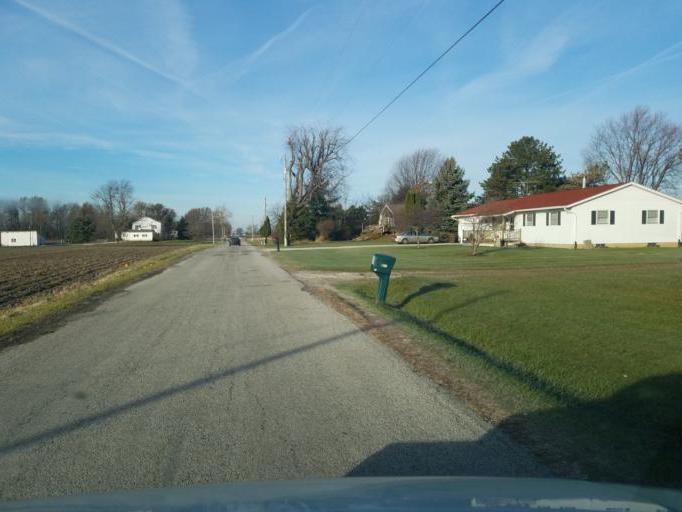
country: US
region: Ohio
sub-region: Morrow County
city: Mount Gilead
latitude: 40.6307
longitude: -82.9000
